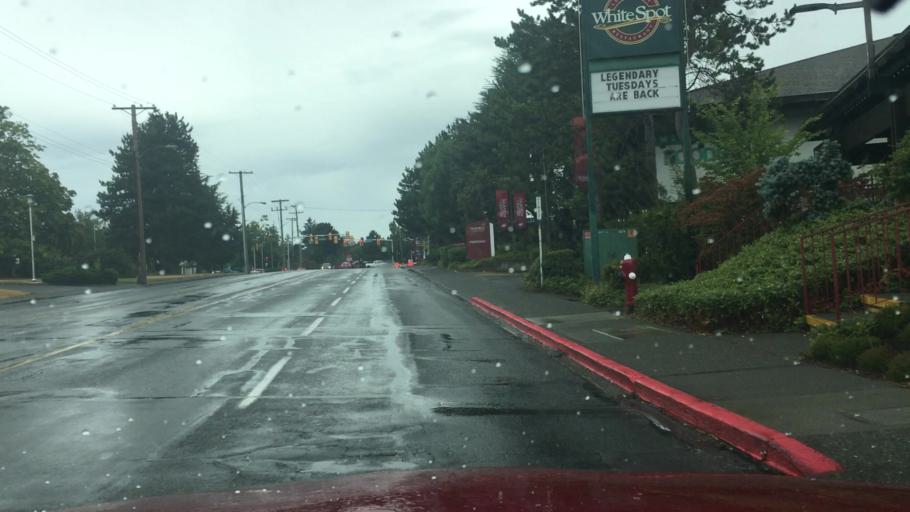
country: CA
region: British Columbia
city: Victoria
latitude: 48.4686
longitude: -123.3633
